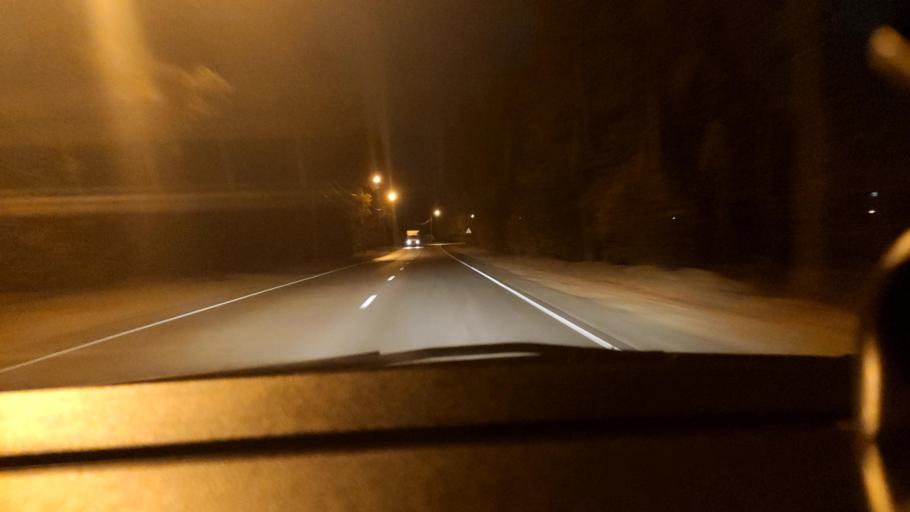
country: RU
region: Voronezj
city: Pridonskoy
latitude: 51.6276
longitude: 39.0818
